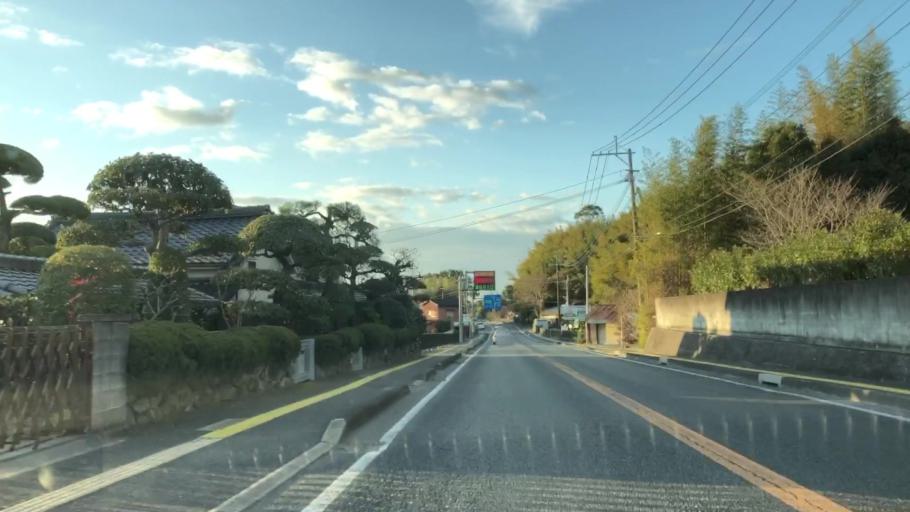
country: JP
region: Fukuoka
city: Nakatsu
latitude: 33.5375
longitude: 131.3008
